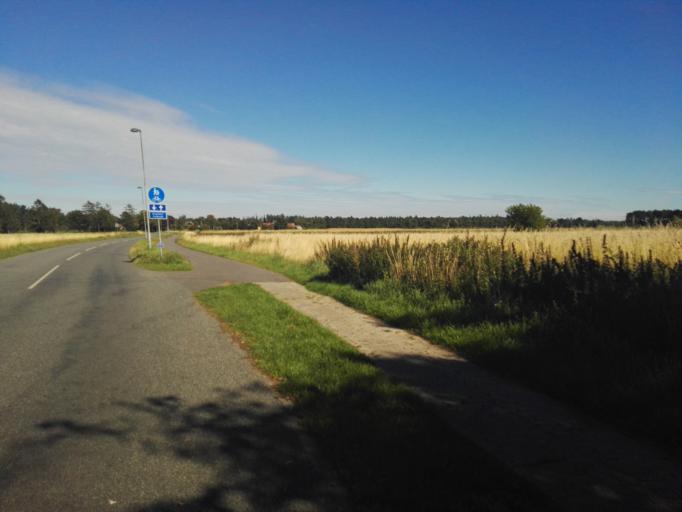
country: DK
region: Zealand
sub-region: Odsherred Kommune
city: Nykobing Sjaelland
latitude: 55.9264
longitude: 11.6852
